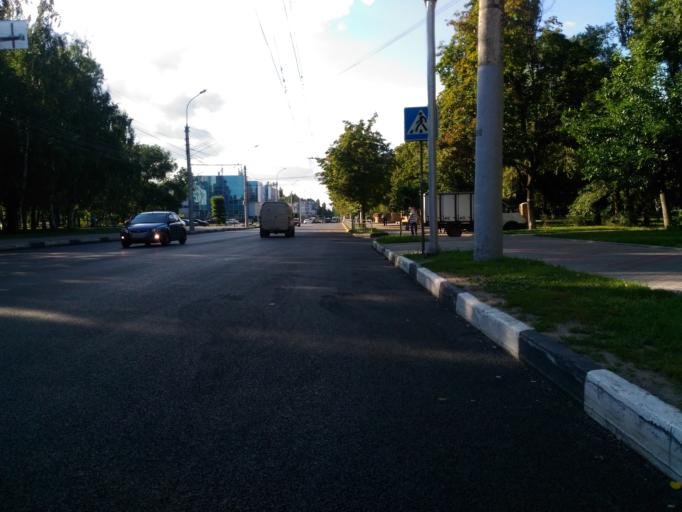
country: RU
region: Voronezj
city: Voronezh
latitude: 51.6510
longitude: 39.1518
